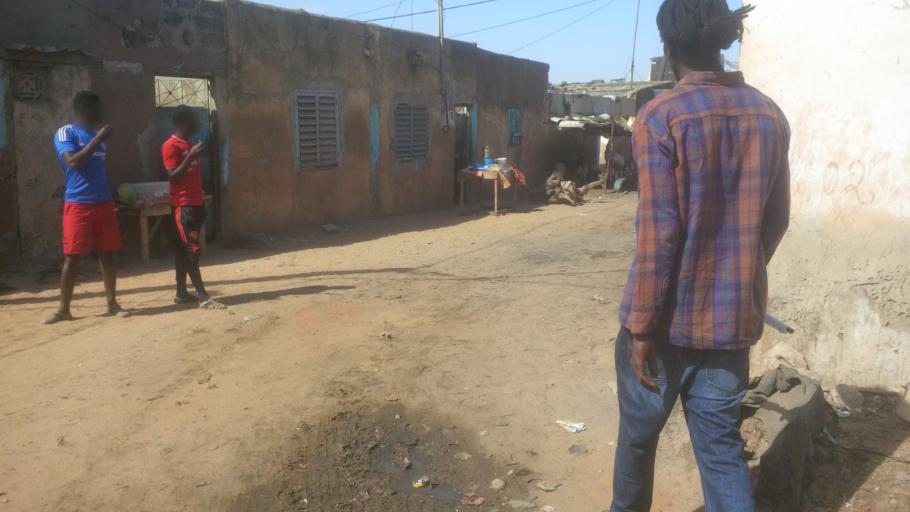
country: SN
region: Dakar
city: Pikine
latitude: 14.7746
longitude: -17.3725
